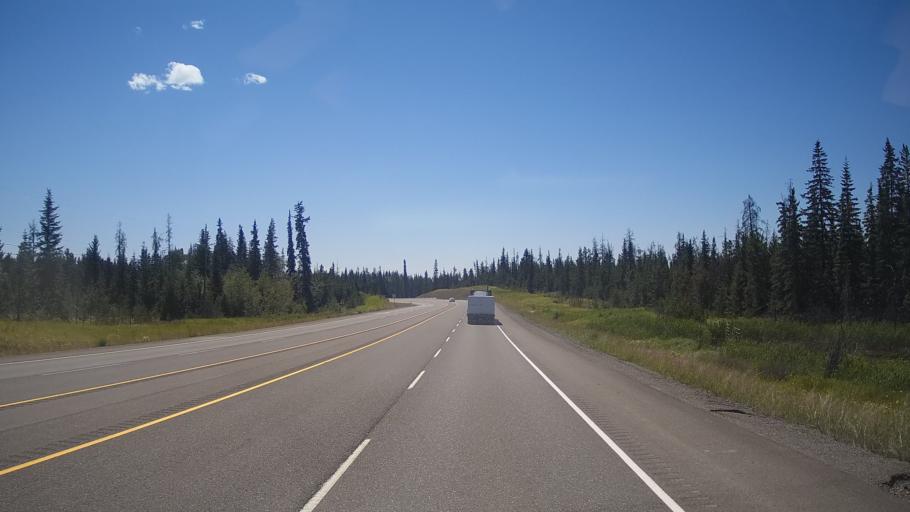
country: CA
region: British Columbia
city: Cache Creek
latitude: 51.3990
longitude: -121.3735
